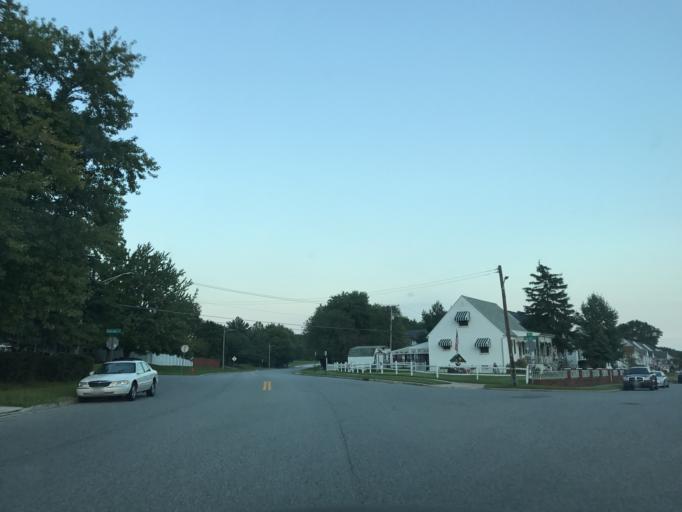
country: US
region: Maryland
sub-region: Baltimore County
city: Dundalk
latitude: 39.2789
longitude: -76.5245
